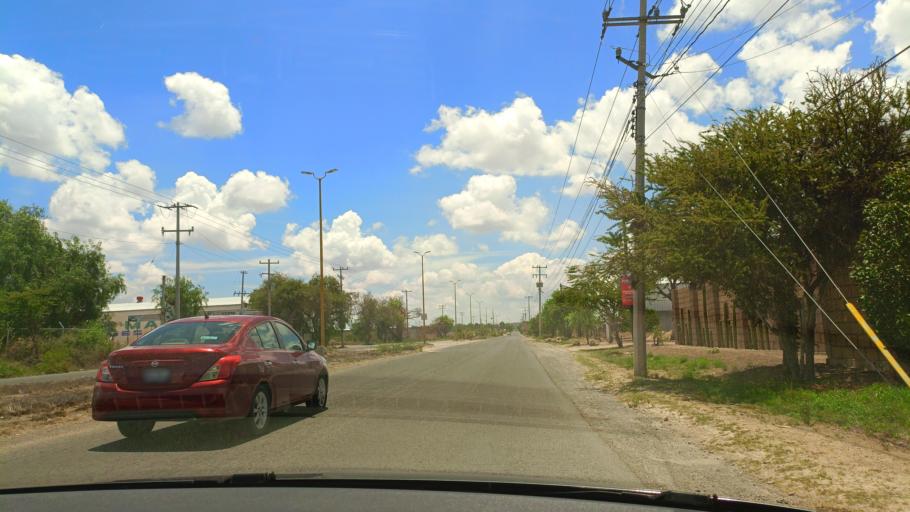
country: MX
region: Guanajuato
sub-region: San Luis de la Paz
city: San Ignacio
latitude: 21.2875
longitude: -100.5514
